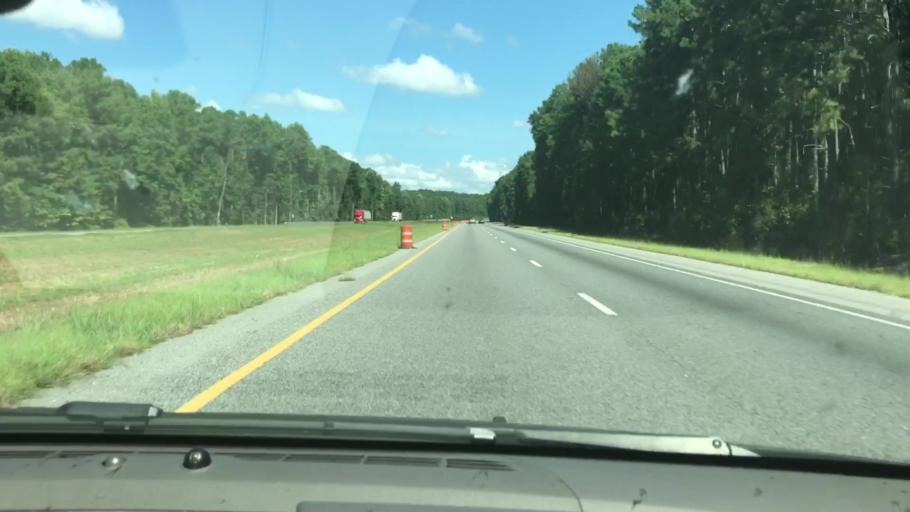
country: US
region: Georgia
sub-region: Harris County
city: Hamilton
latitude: 32.7114
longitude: -85.0137
